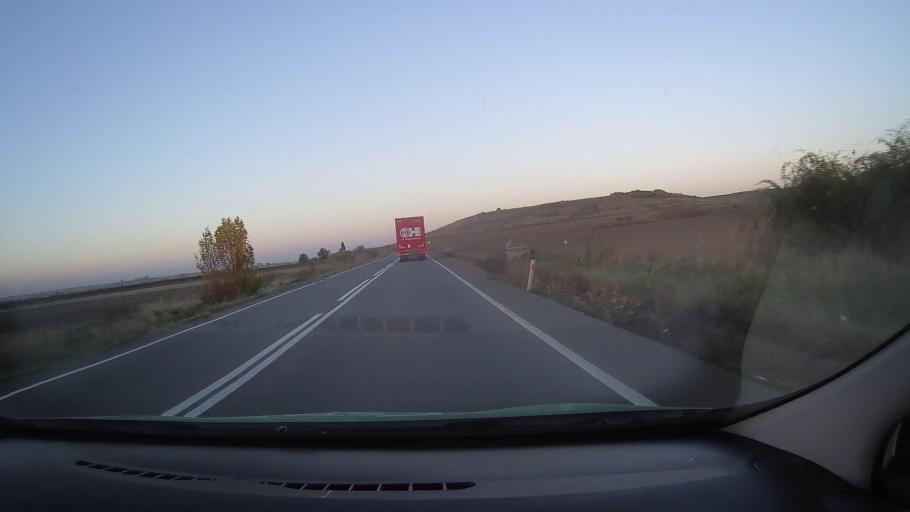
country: RO
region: Bihor
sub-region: Comuna Cherechiu
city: Cherechiu
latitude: 47.4005
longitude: 22.1640
